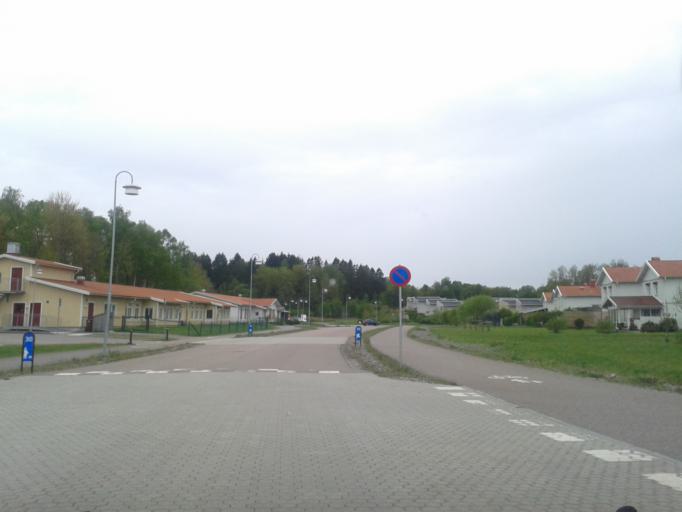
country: SE
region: Vaestra Goetaland
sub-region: Kungalvs Kommun
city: Kungalv
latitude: 57.8953
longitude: 11.9519
